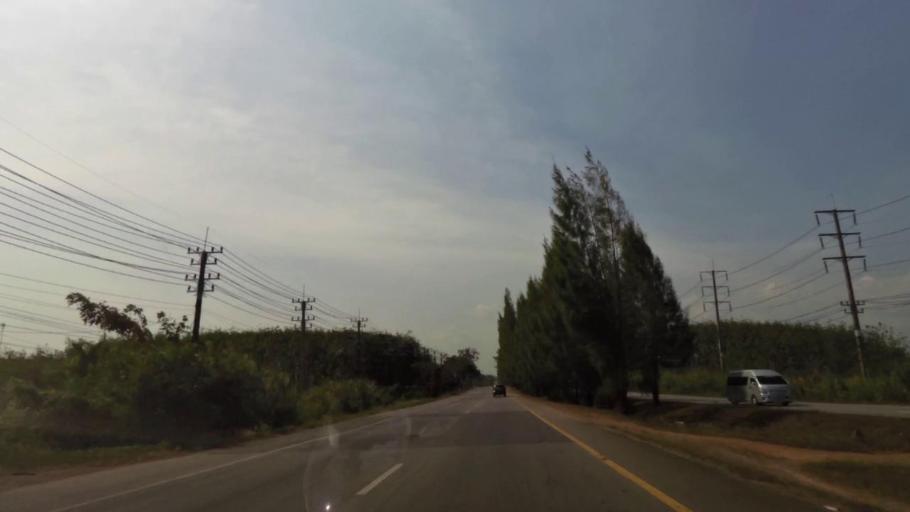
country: TH
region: Chanthaburi
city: Chanthaburi
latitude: 12.6634
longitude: 102.1176
